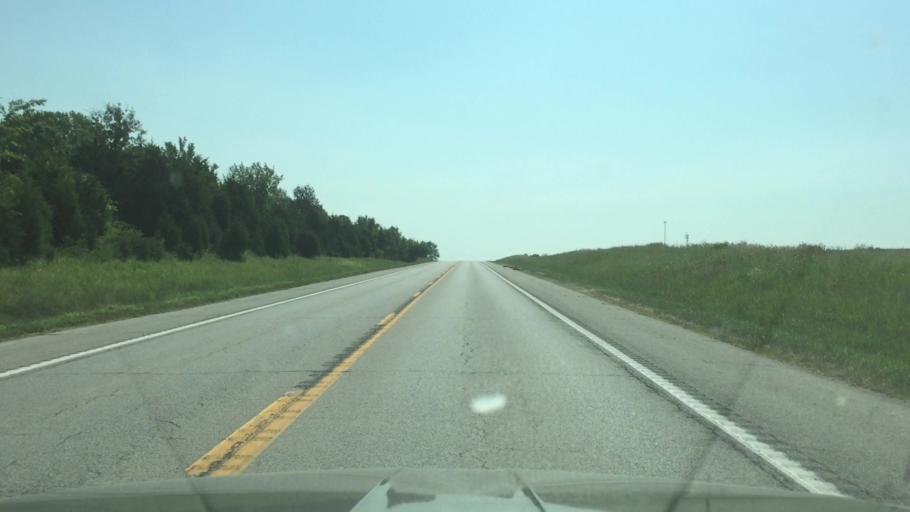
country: US
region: Missouri
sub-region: Pettis County
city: Sedalia
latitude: 38.6944
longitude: -93.1146
